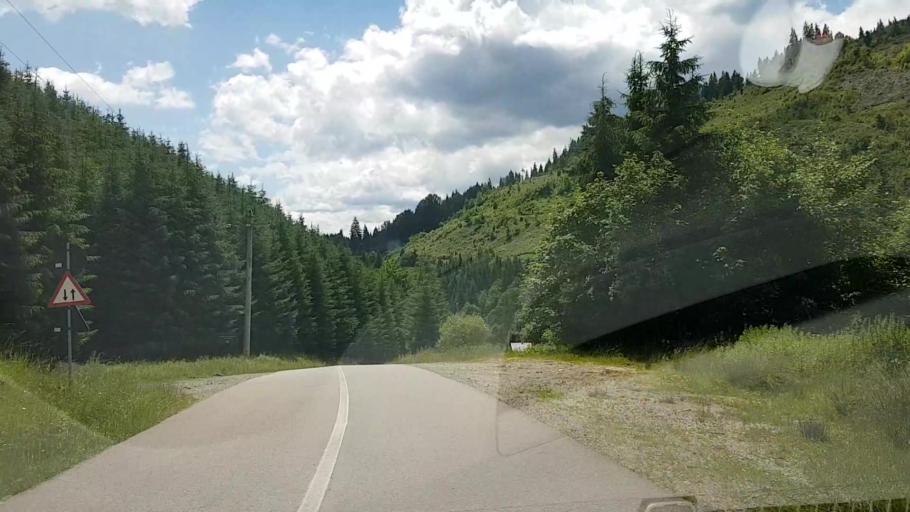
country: RO
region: Suceava
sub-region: Comuna Crucea
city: Crucea
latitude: 47.4233
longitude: 25.5792
